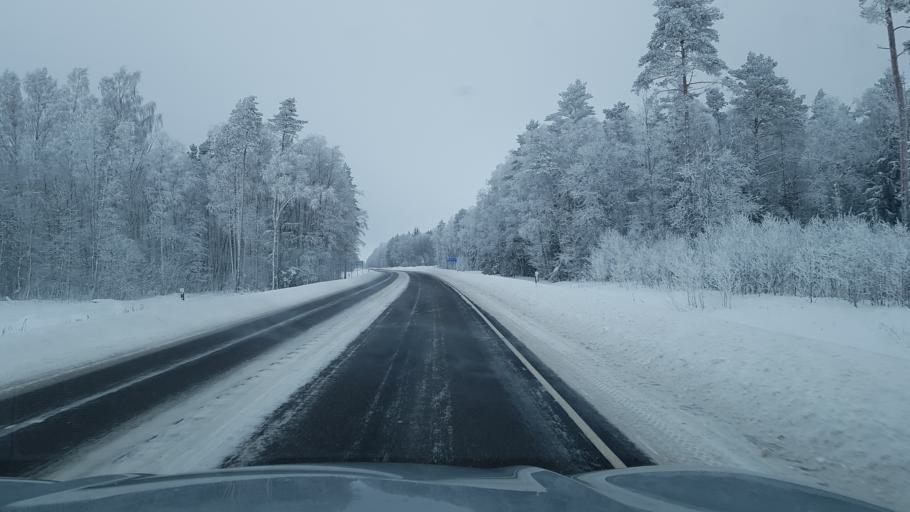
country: EE
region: Ida-Virumaa
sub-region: Johvi vald
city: Johvi
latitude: 59.2931
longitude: 27.3990
